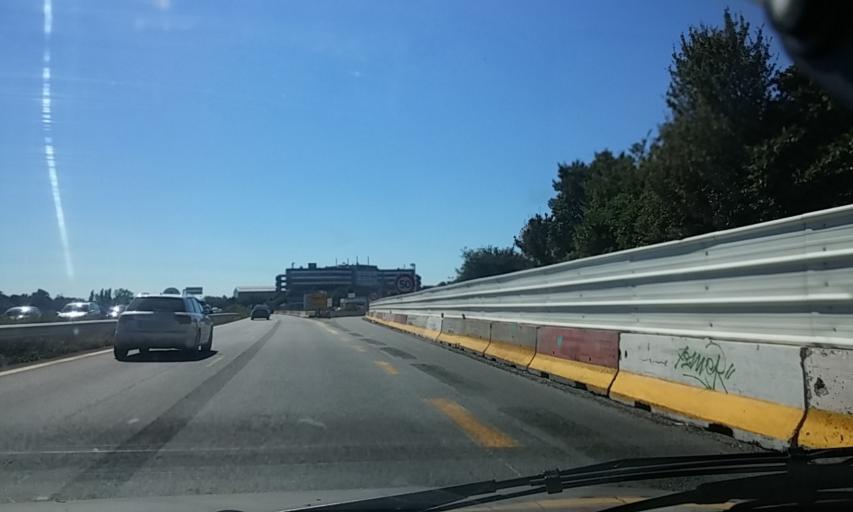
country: FR
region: Ile-de-France
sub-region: Departement de Seine-et-Marne
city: Pontault-Combault
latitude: 48.7943
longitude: 2.6201
